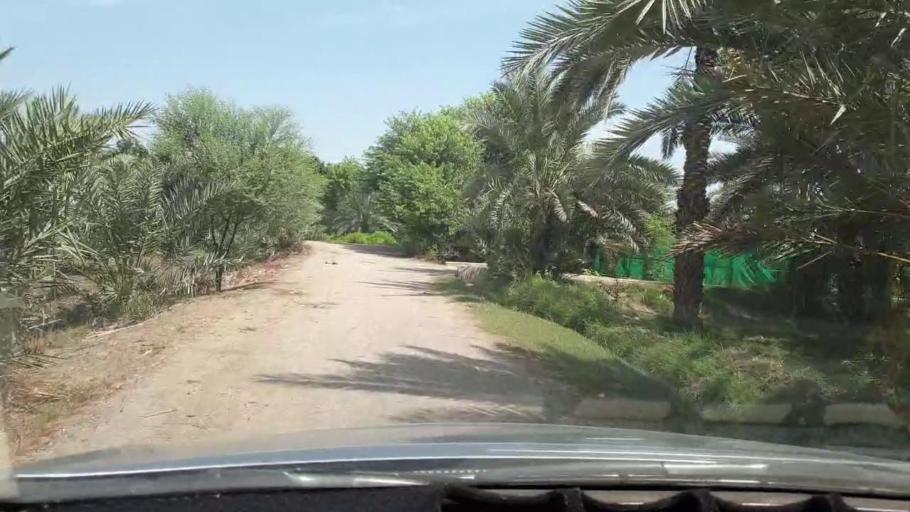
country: PK
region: Sindh
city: Khairpur
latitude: 27.4988
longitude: 68.7502
